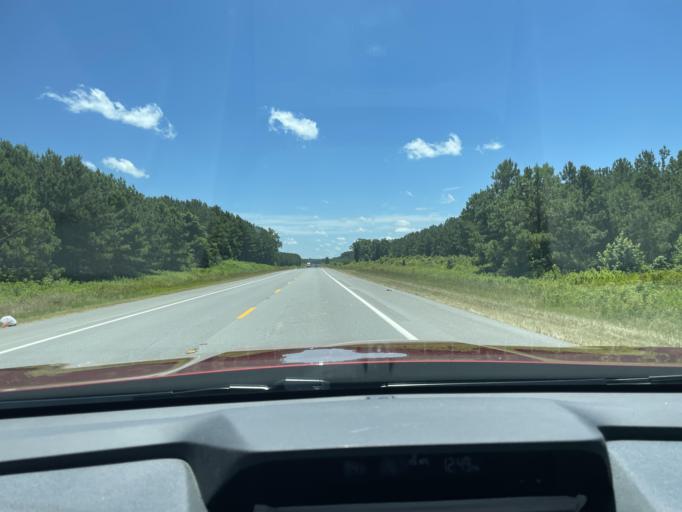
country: US
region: Arkansas
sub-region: Lincoln County
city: Star City
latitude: 33.9564
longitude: -91.9061
